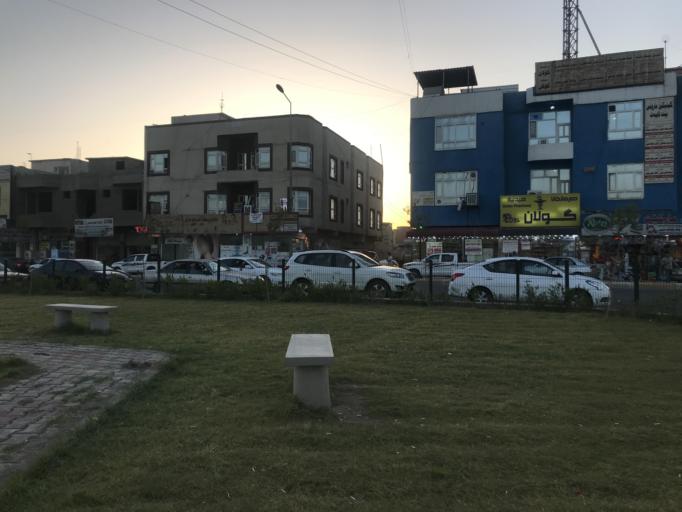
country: IQ
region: Dahuk
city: Saymayl
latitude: 36.8602
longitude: 42.8362
